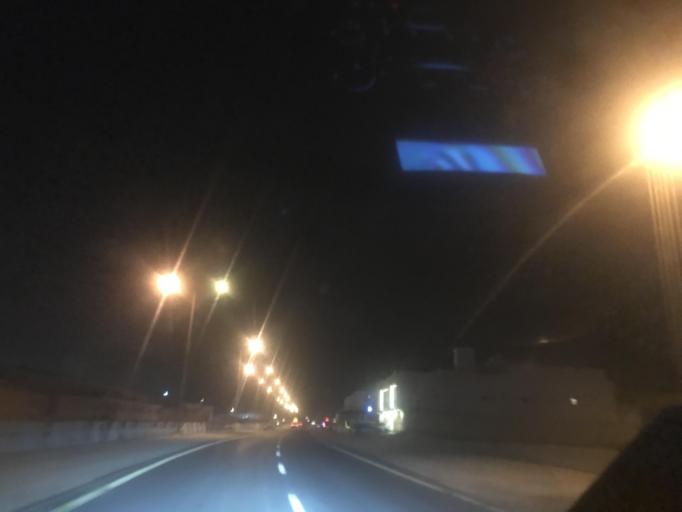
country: SA
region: Ar Riyad
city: Riyadh
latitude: 24.7655
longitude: 46.5946
